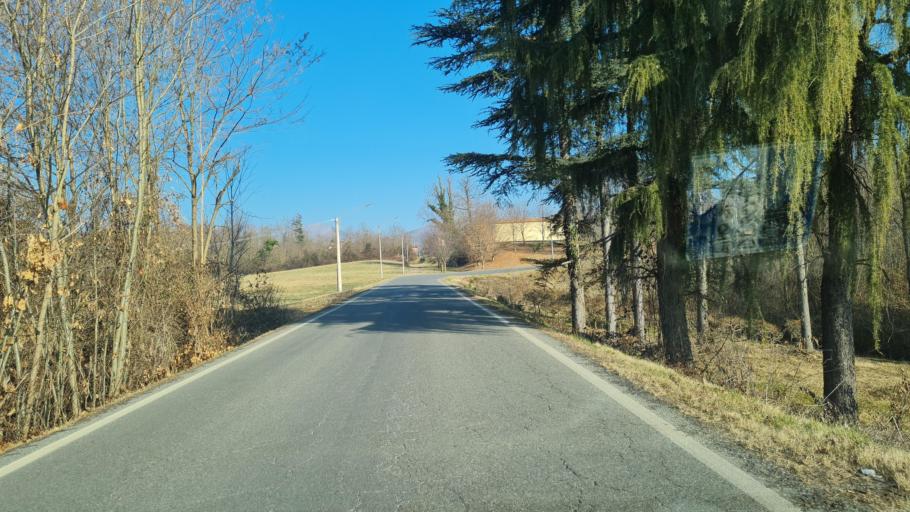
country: IT
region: Piedmont
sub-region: Provincia di Biella
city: Piatto
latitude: 45.5830
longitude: 8.1369
